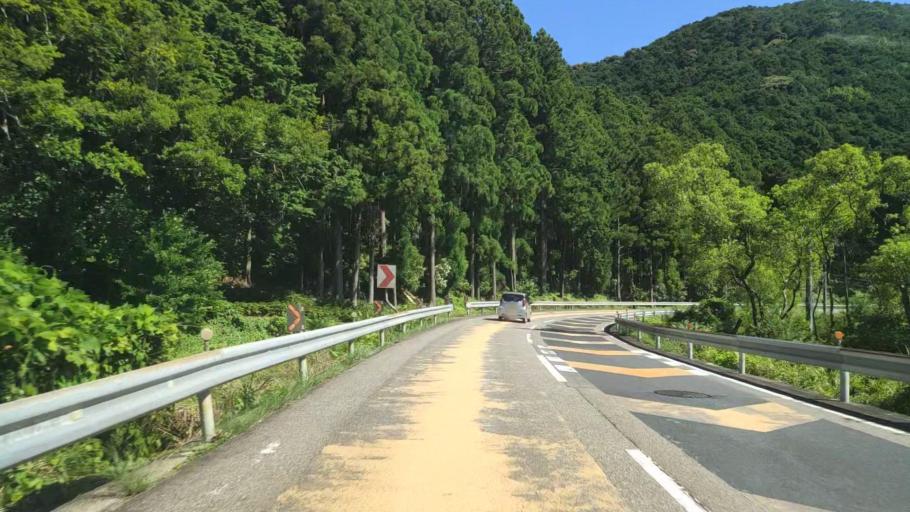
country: JP
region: Wakayama
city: Shingu
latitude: 33.5475
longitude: 135.8766
